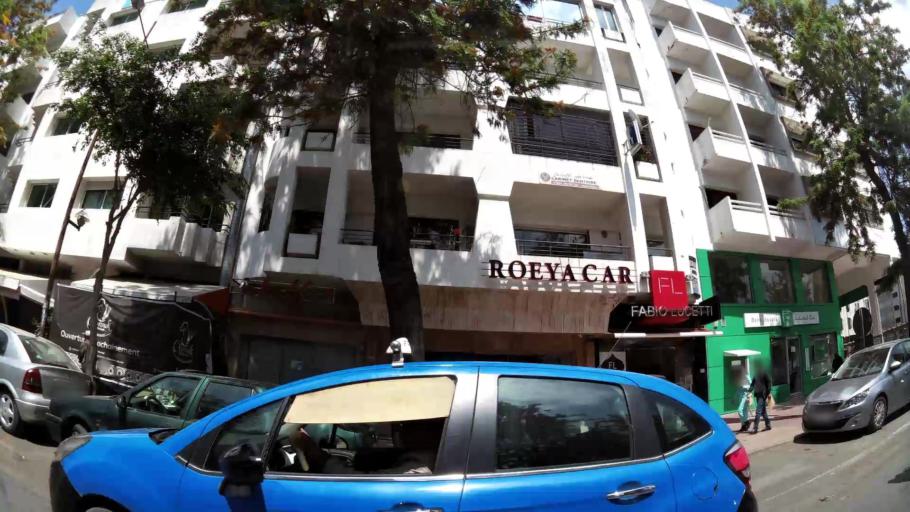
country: MA
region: Rabat-Sale-Zemmour-Zaer
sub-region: Rabat
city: Rabat
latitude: 34.0015
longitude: -6.8504
